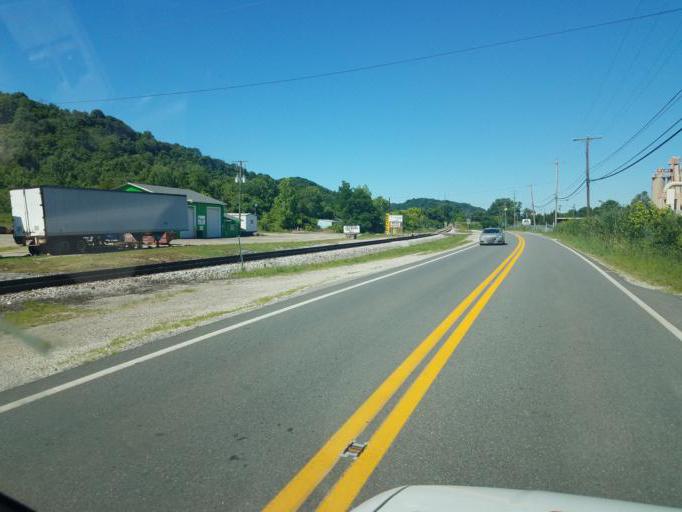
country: US
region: West Virginia
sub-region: Cabell County
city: Pea Ridge
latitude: 38.4318
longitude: -82.3691
